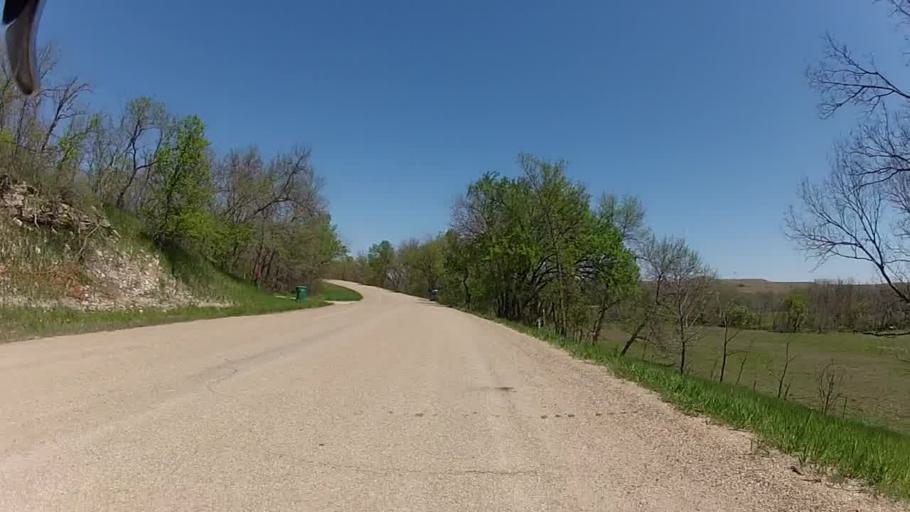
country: US
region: Kansas
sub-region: Riley County
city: Ogden
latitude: 38.9987
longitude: -96.5975
